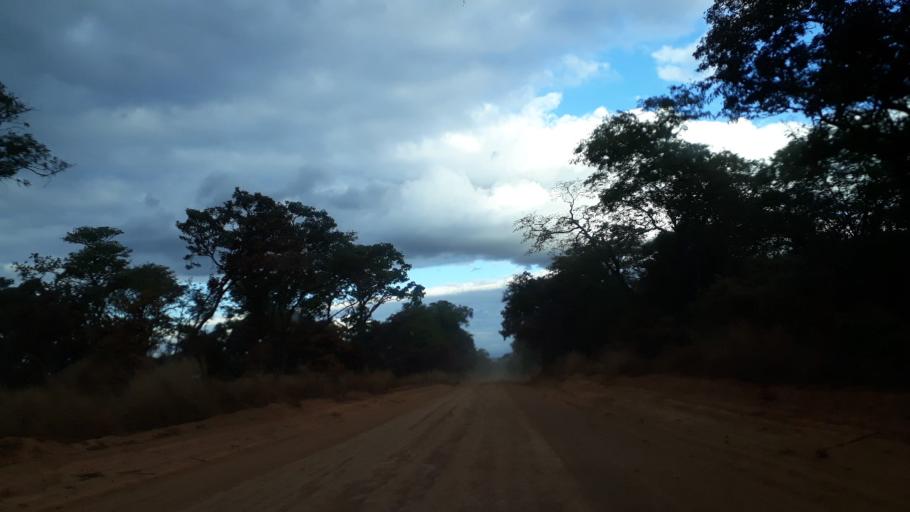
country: ZM
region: Copperbelt
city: Mufulira
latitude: -12.3531
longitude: 28.1016
